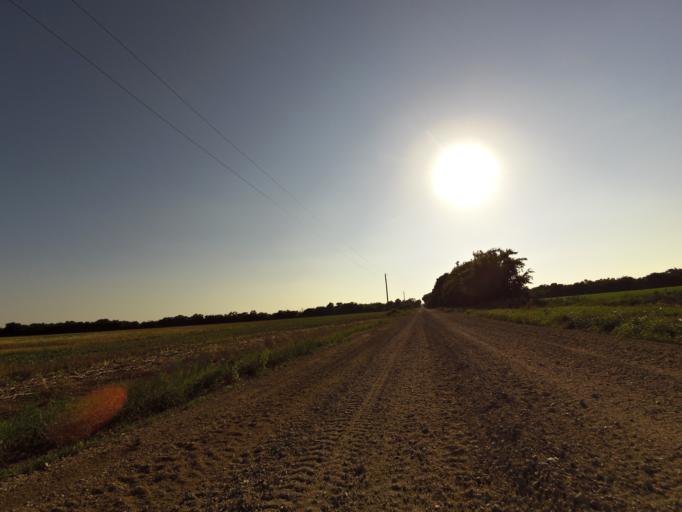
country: US
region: Kansas
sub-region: McPherson County
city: Inman
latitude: 38.1883
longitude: -97.8572
